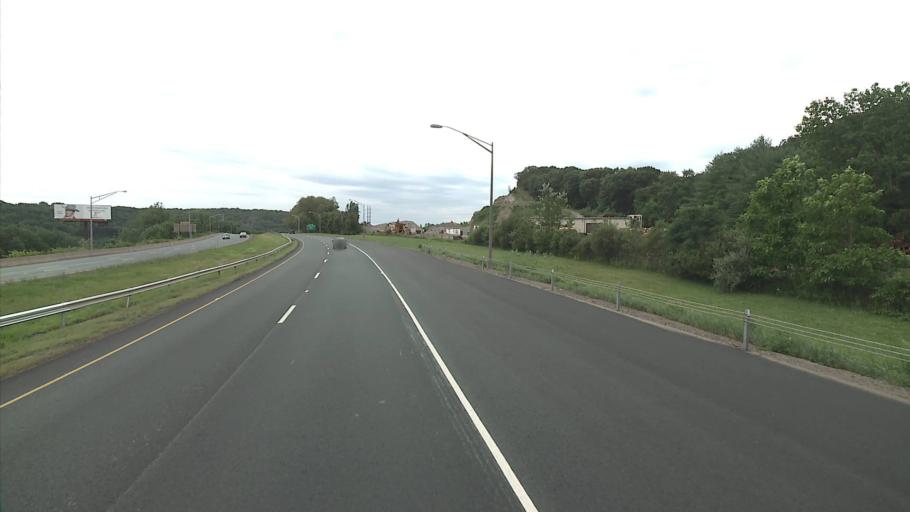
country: US
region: Connecticut
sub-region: New Haven County
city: Waterbury
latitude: 41.5294
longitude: -73.0448
